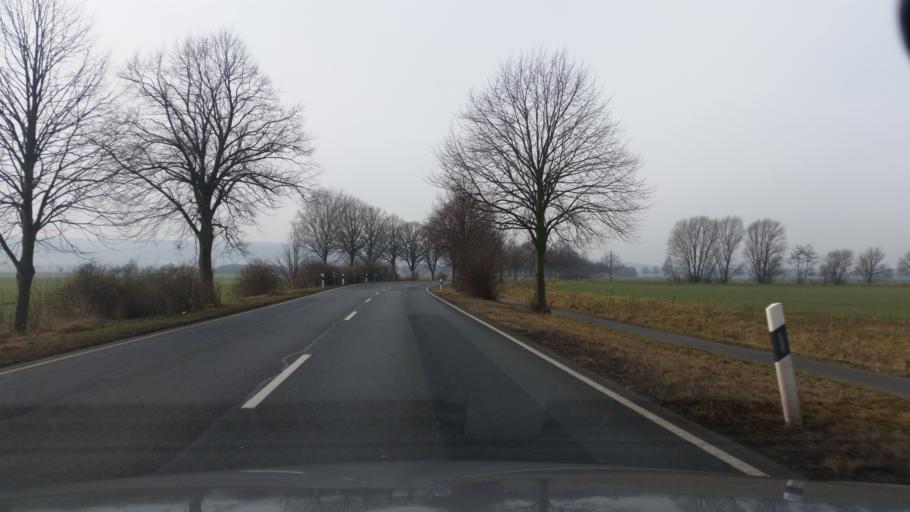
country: DE
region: Lower Saxony
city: Grossgoltern
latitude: 52.3352
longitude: 9.4806
